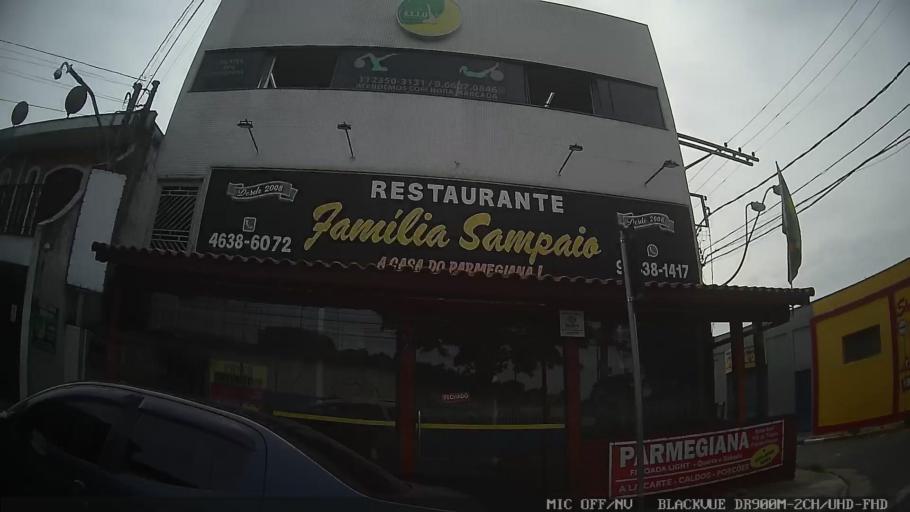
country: BR
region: Sao Paulo
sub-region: Poa
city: Poa
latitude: -23.5161
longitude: -46.3421
